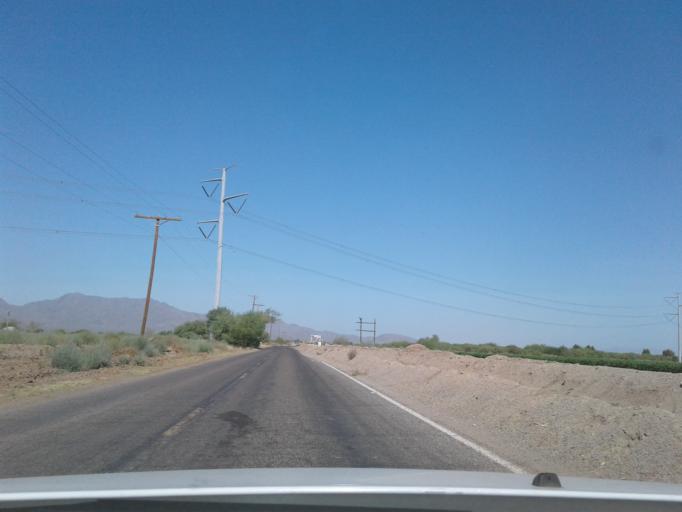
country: US
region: Arizona
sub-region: Maricopa County
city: Laveen
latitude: 33.3339
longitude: -112.1763
